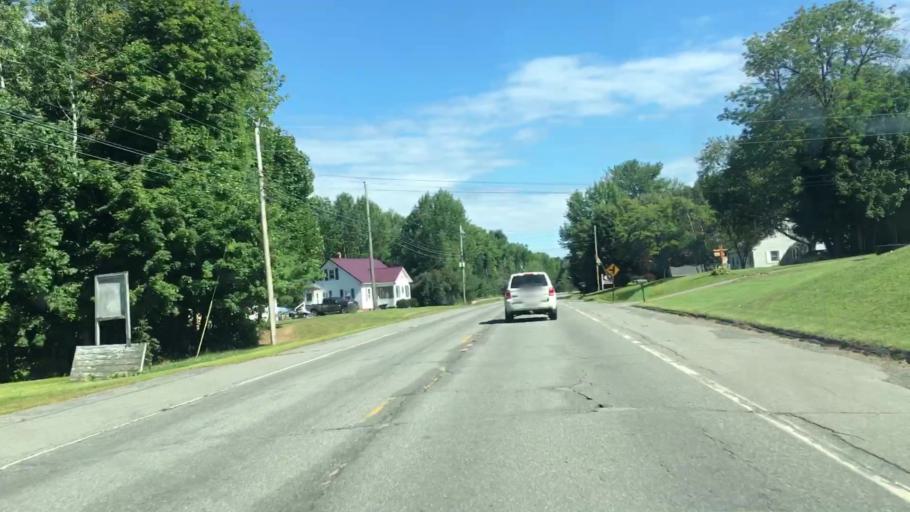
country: US
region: Maine
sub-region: Penobscot County
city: Dexter
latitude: 45.0453
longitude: -69.2722
